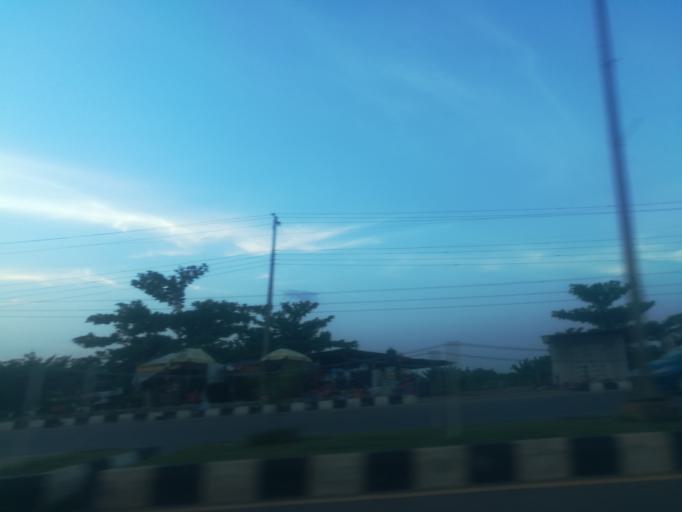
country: NG
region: Ogun
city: Abeokuta
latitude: 7.1288
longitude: 3.3594
